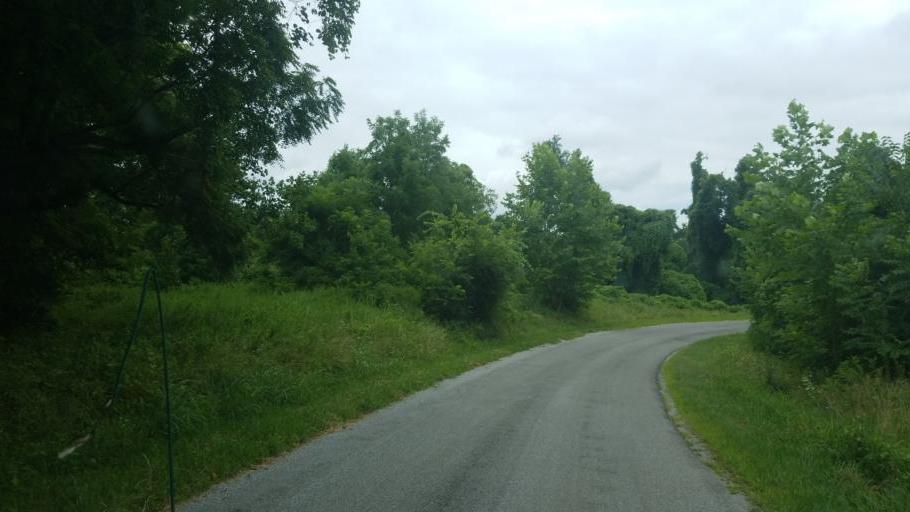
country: US
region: Illinois
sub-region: Jackson County
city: Murphysboro
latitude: 37.6858
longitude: -89.3852
